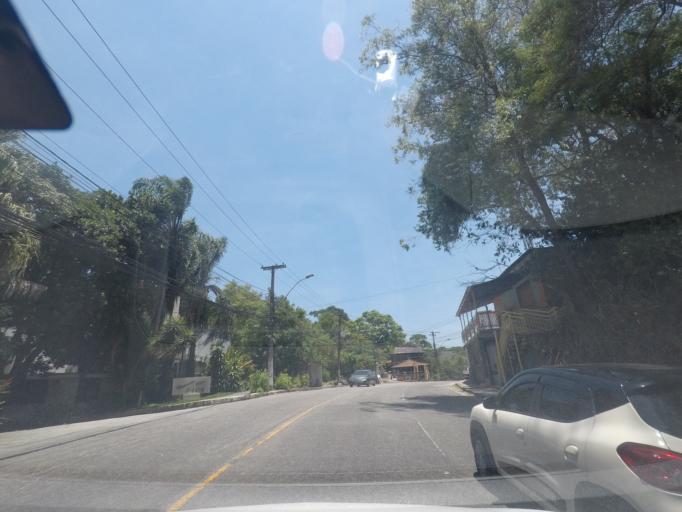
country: BR
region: Rio de Janeiro
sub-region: Niteroi
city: Niteroi
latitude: -22.9176
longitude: -43.0650
